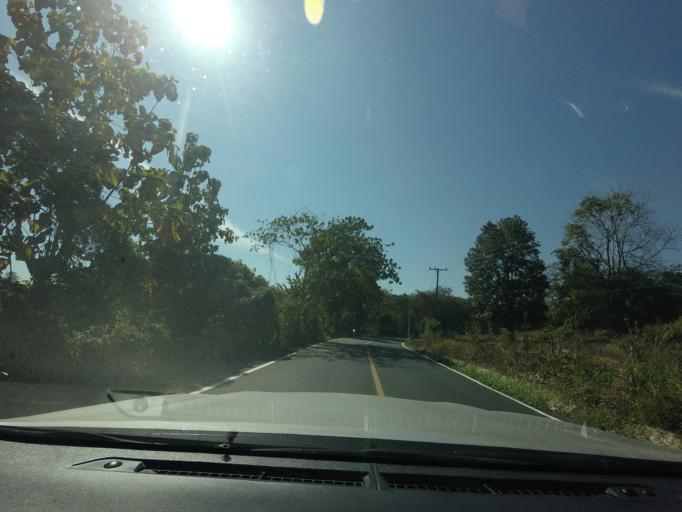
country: TH
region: Mae Hong Son
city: Wiang Nuea
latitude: 19.3795
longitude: 98.4352
